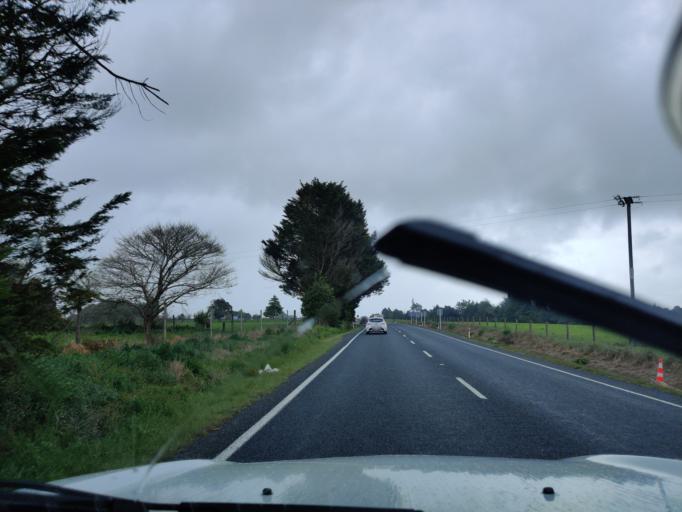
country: NZ
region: Waikato
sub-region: South Waikato District
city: Tokoroa
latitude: -38.0028
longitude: 175.9124
